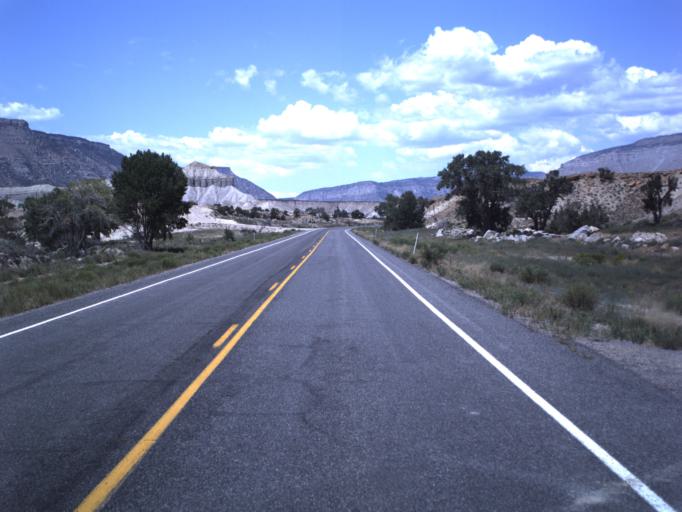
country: US
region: Utah
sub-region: Emery County
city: Orangeville
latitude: 39.2345
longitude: -111.0833
